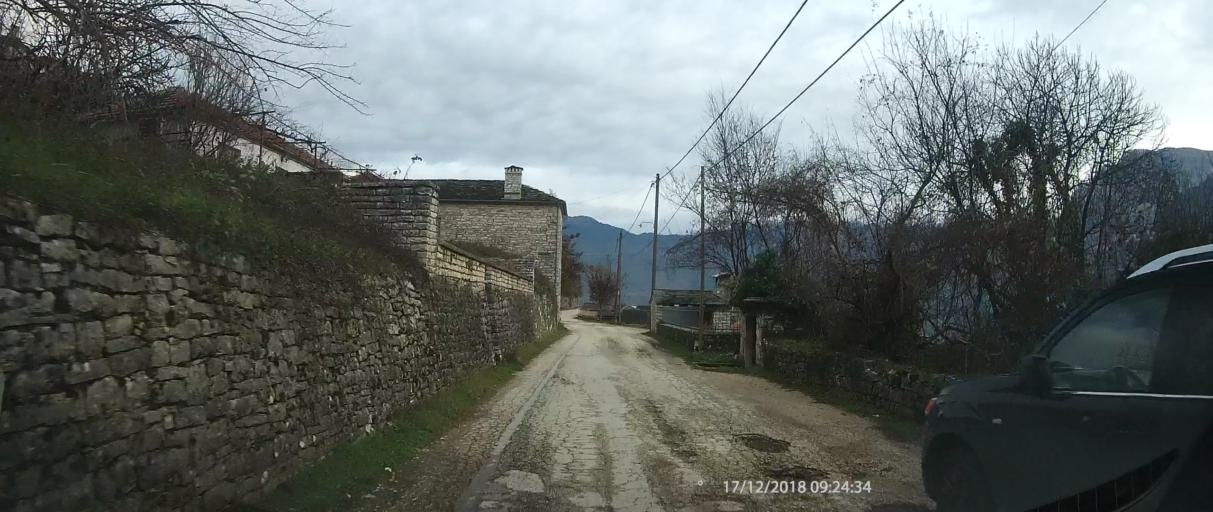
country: GR
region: Epirus
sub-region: Nomos Ioanninon
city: Kalpaki
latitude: 39.9349
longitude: 20.6723
